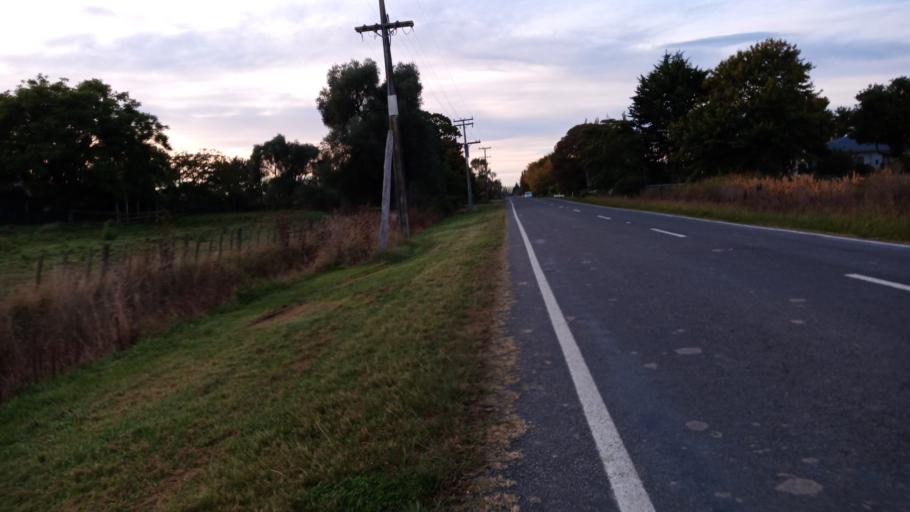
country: NZ
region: Gisborne
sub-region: Gisborne District
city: Gisborne
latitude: -38.6443
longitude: 177.9410
